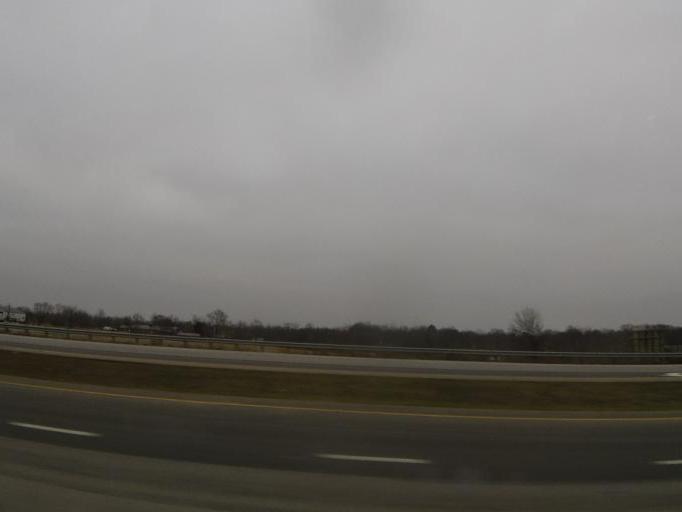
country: US
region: Missouri
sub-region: Ralls County
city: New London
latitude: 39.5927
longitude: -91.4068
